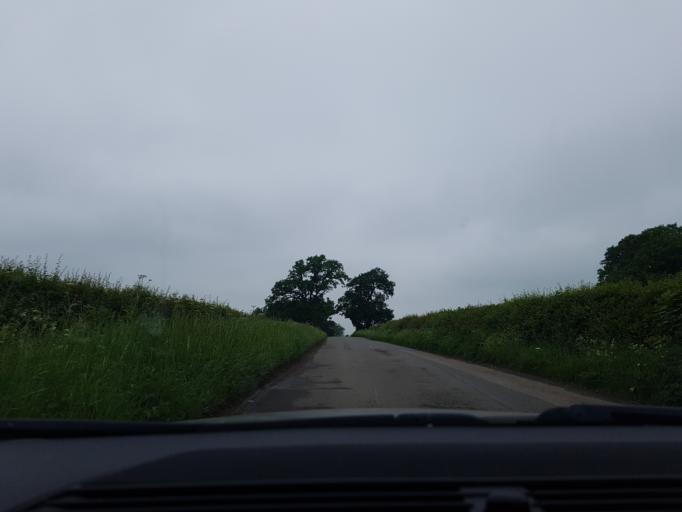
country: GB
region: England
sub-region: Buckinghamshire
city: Steeple Claydon
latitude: 51.9328
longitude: -0.9724
